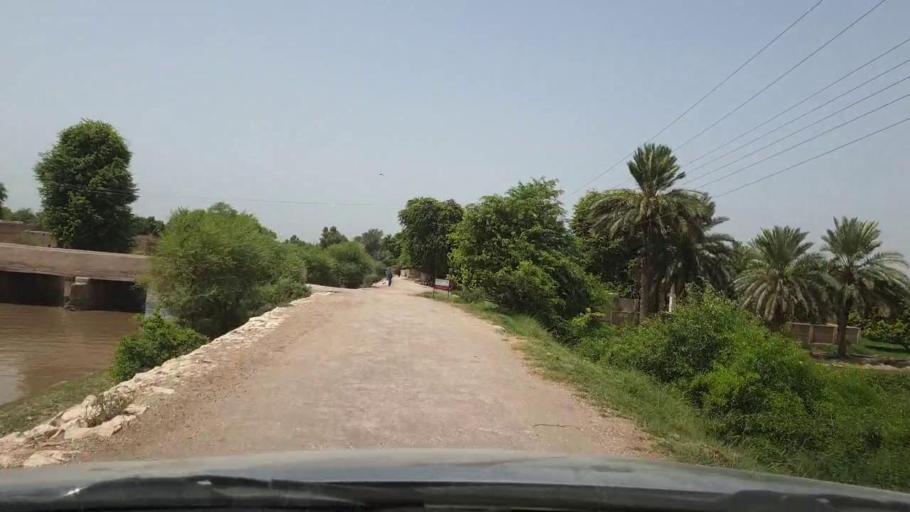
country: PK
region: Sindh
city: Pano Aqil
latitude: 27.9179
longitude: 69.1588
